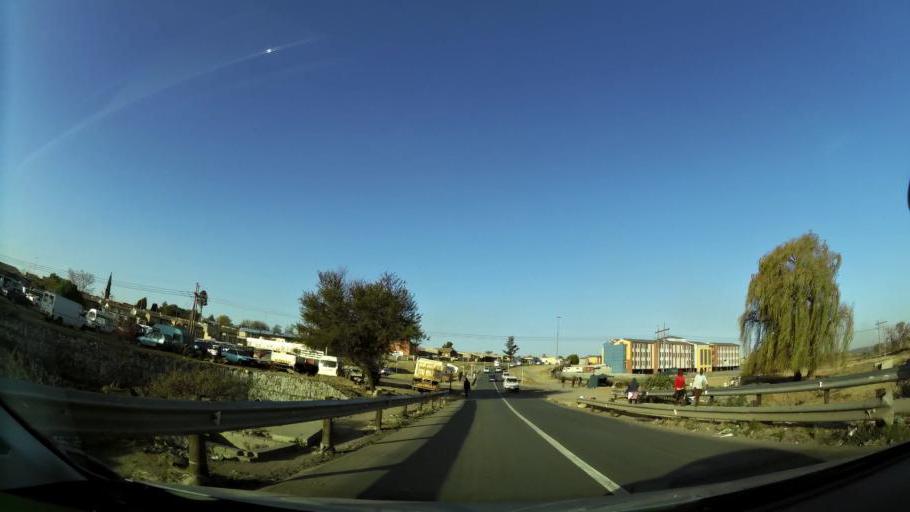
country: ZA
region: Gauteng
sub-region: Ekurhuleni Metropolitan Municipality
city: Tembisa
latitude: -26.0251
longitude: 28.2068
